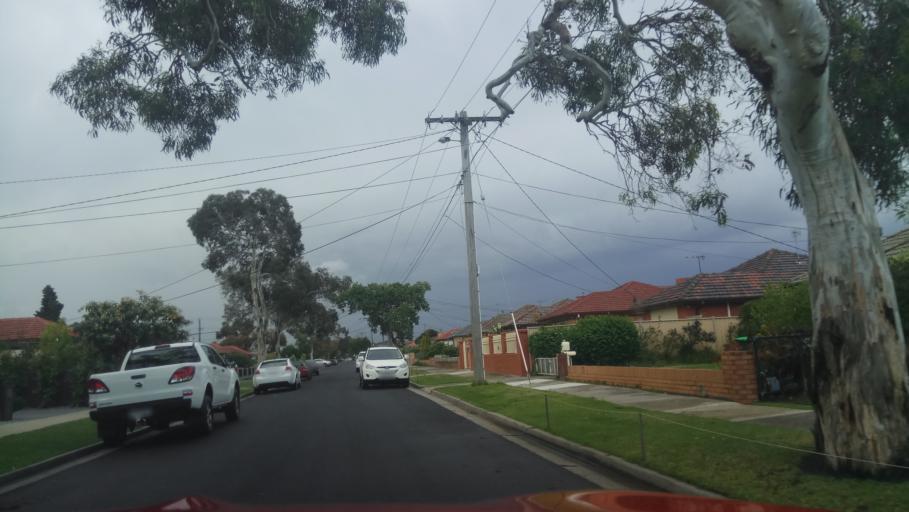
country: AU
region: Victoria
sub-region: Hobsons Bay
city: Altona North
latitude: -37.8447
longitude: 144.8471
